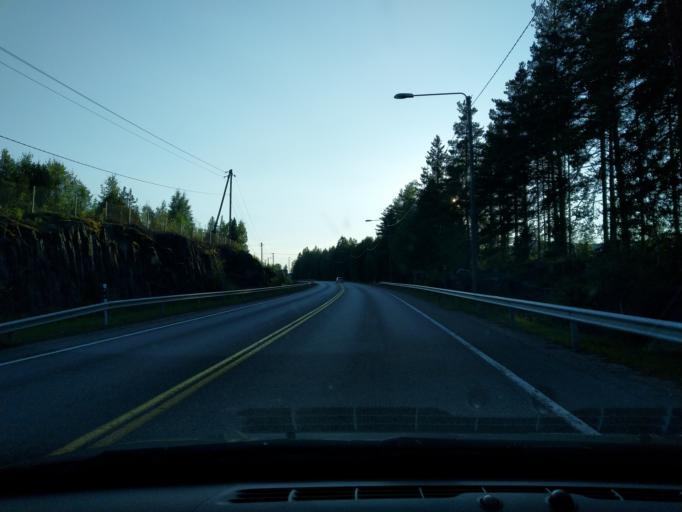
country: FI
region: Uusimaa
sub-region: Helsinki
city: Maentsaelae
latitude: 60.6283
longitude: 25.2801
